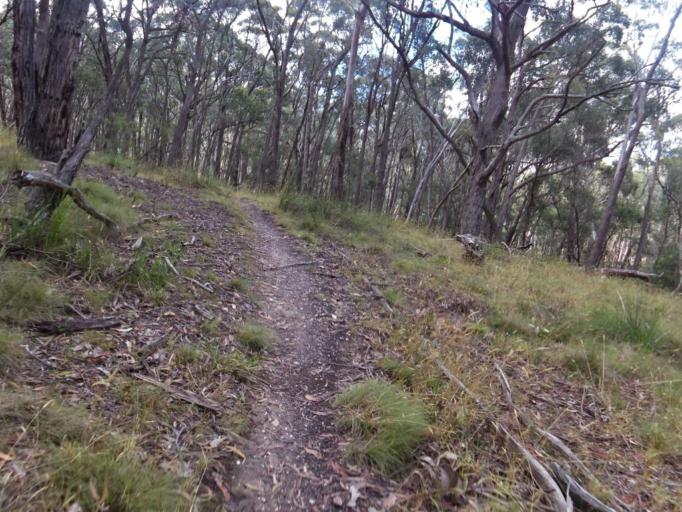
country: AU
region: Victoria
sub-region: Melton
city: Melton West
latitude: -37.4823
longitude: 144.5361
